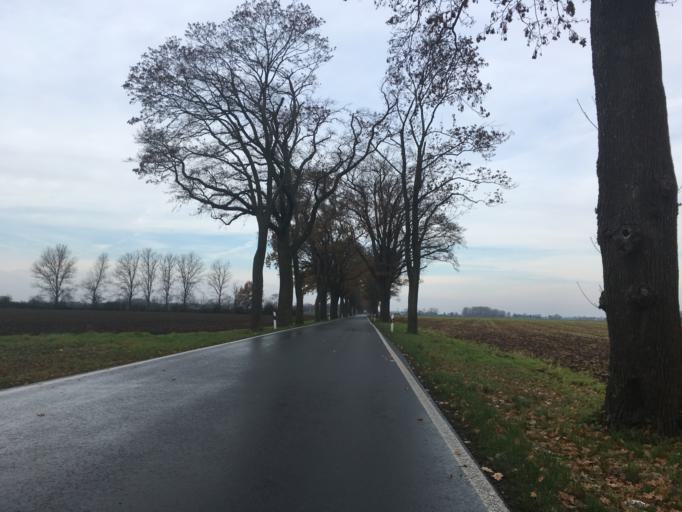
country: DE
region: Brandenburg
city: Letschin
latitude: 52.7021
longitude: 14.3958
